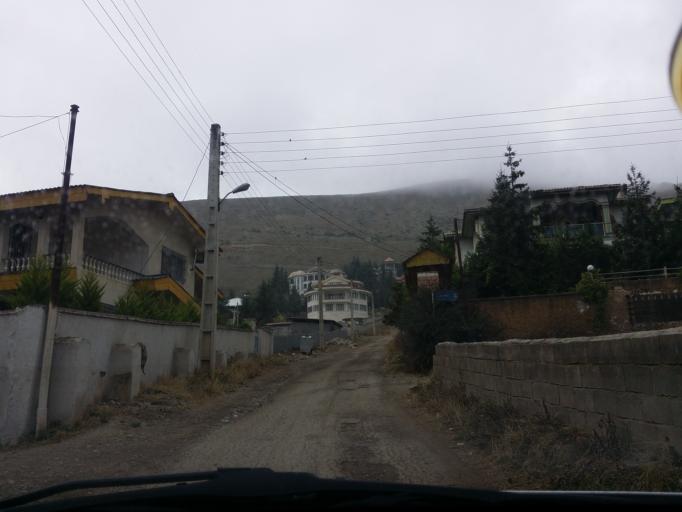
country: IR
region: Mazandaran
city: `Abbasabad
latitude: 36.5091
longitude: 51.1566
